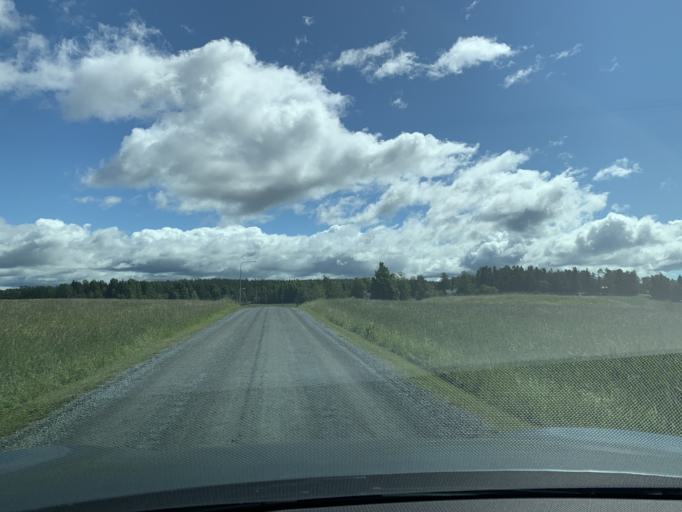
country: SE
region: Jaemtland
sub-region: Krokoms Kommun
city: Krokom
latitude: 63.1476
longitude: 14.3448
